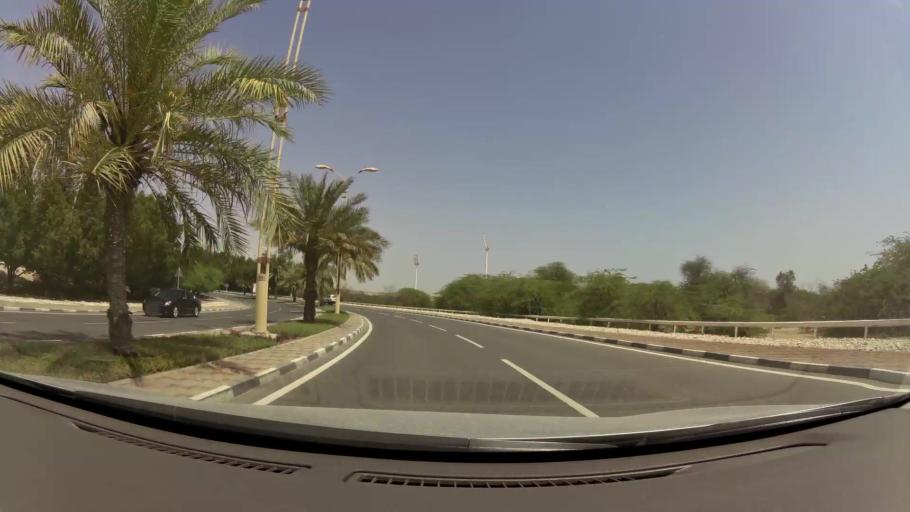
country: QA
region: Baladiyat ad Dawhah
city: Doha
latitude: 25.3724
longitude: 51.4953
